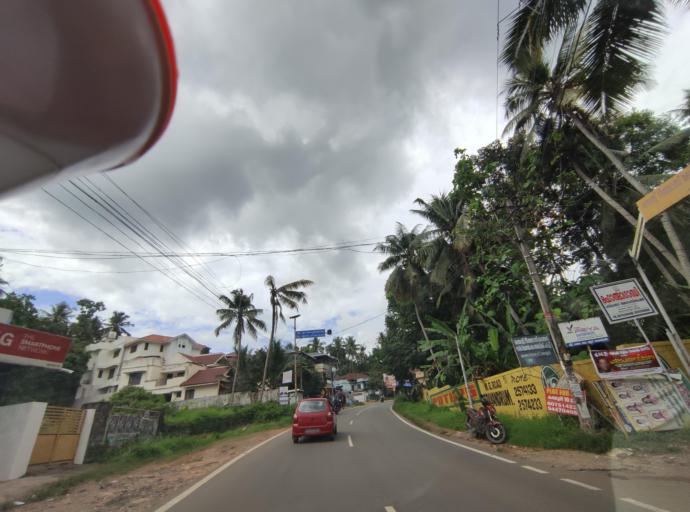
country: IN
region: Kerala
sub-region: Thiruvananthapuram
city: Nedumangad
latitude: 8.5716
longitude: 76.9456
